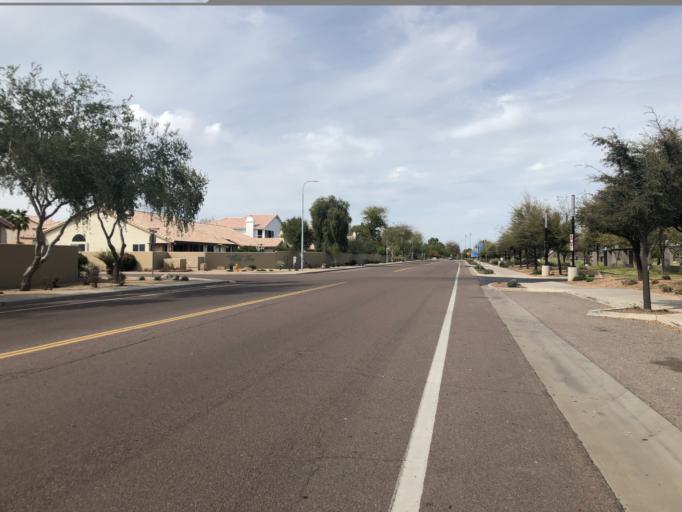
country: US
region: Arizona
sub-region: Maricopa County
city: Guadalupe
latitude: 33.3070
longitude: -111.9198
